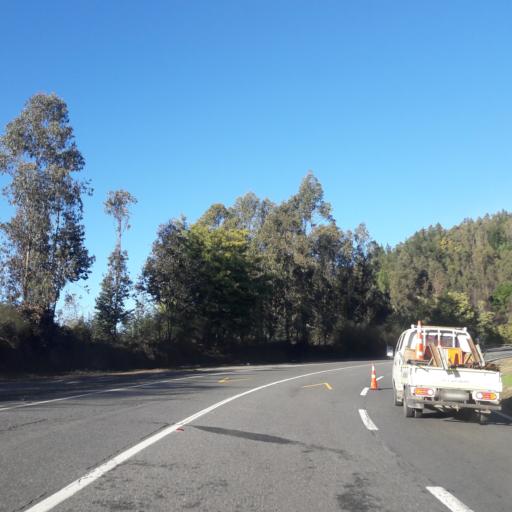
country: CL
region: Biobio
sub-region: Provincia de Biobio
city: La Laja
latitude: -37.2598
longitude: -72.9606
